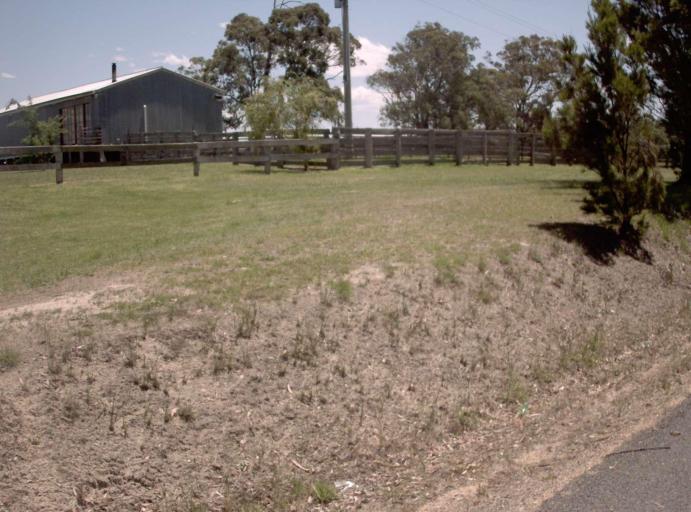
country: AU
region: Victoria
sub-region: East Gippsland
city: Lakes Entrance
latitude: -37.8331
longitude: 148.0309
